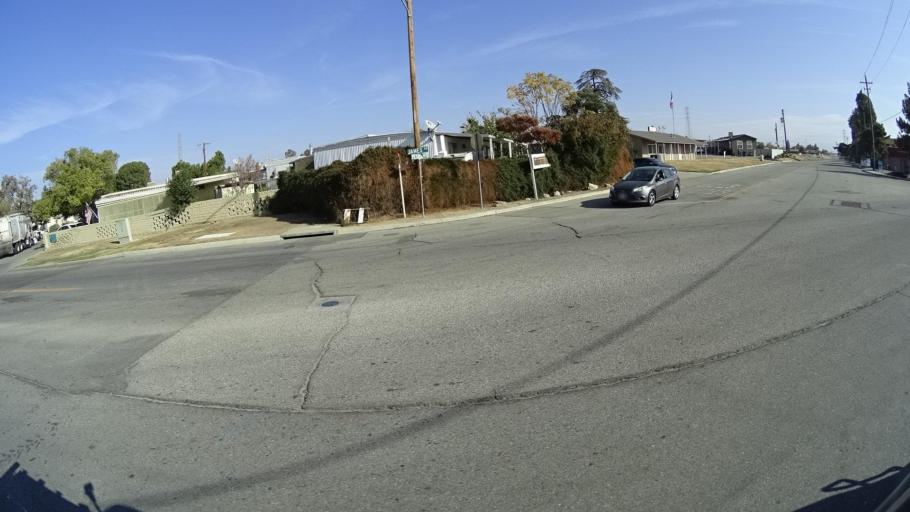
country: US
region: California
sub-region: Kern County
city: Oildale
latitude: 35.4485
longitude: -119.0310
